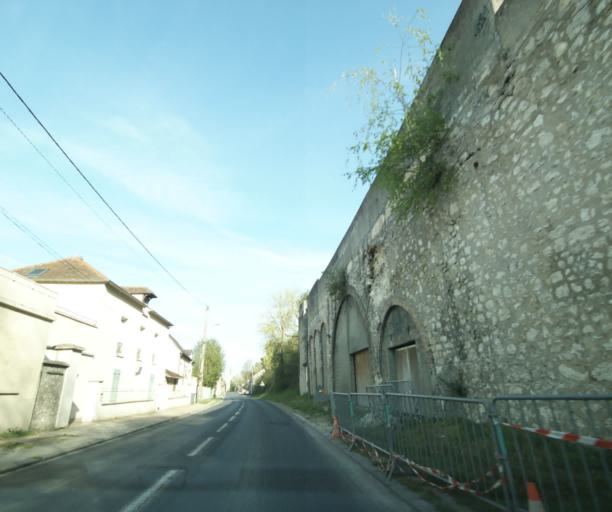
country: FR
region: Ile-de-France
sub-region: Departement de Seine-et-Marne
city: Saint-Mammes
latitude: 48.3787
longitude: 2.8182
